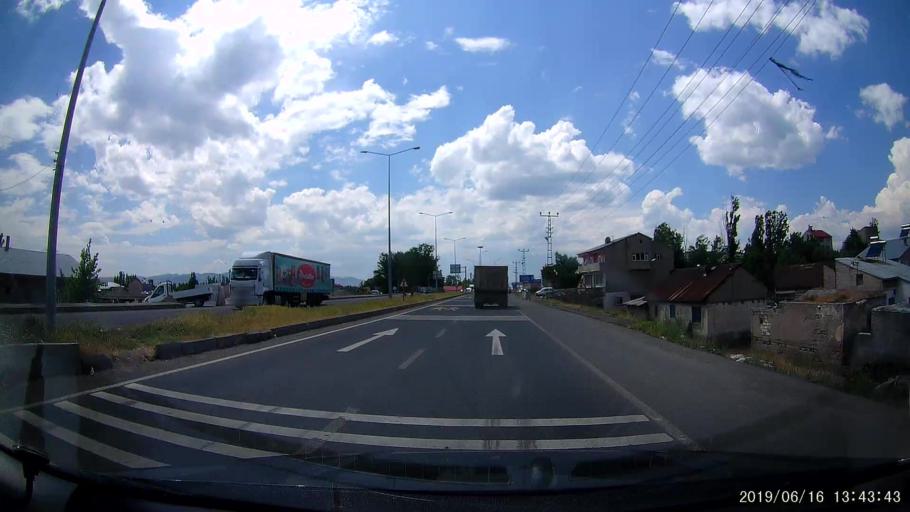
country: TR
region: Agri
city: Agri
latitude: 39.7081
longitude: 43.0509
